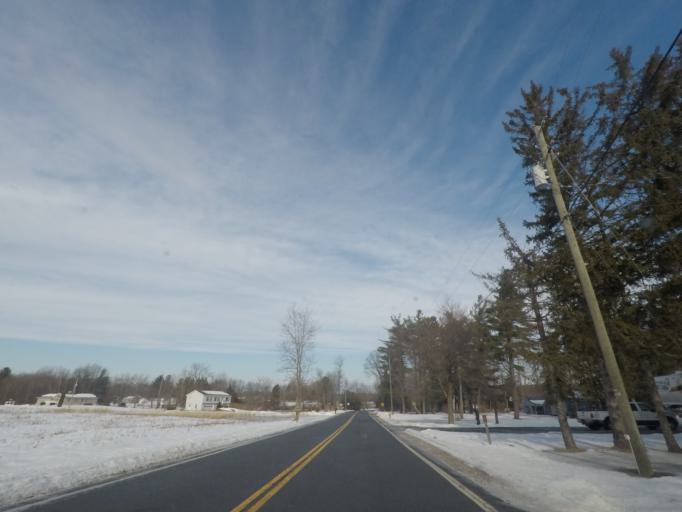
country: US
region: New York
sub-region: Saratoga County
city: Mechanicville
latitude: 42.8566
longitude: -73.7343
